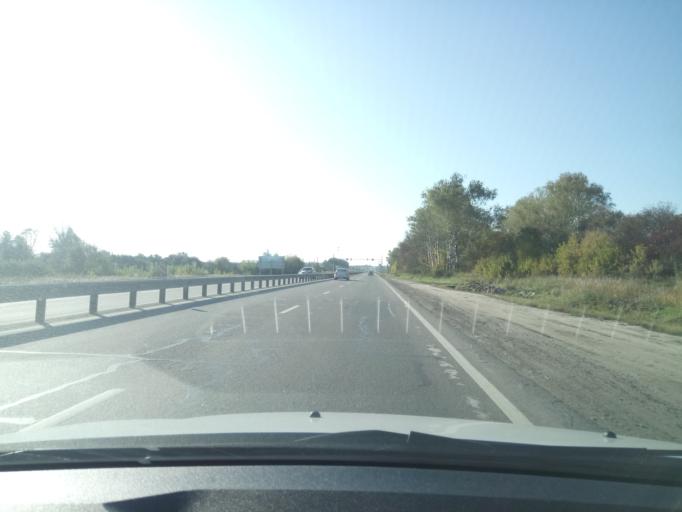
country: RU
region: Nizjnij Novgorod
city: Burevestnik
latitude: 56.1416
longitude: 43.9125
